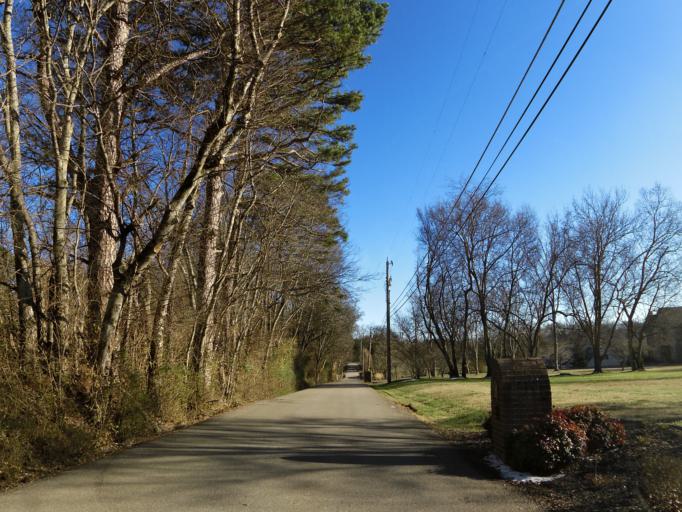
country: US
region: Tennessee
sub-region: Knox County
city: Knoxville
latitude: 35.8858
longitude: -83.9711
